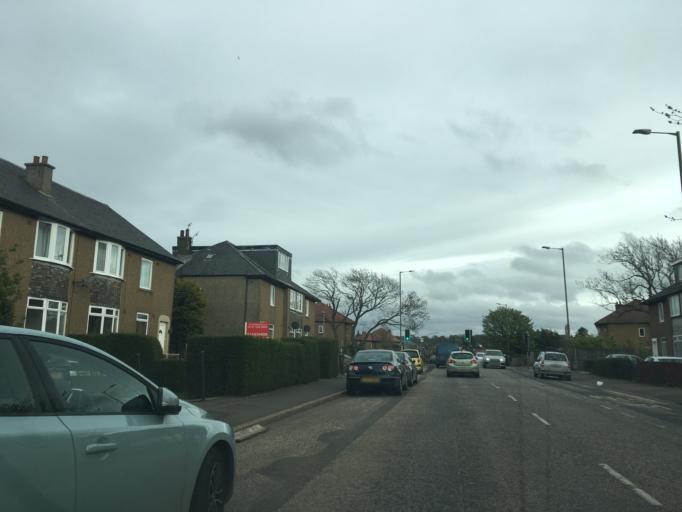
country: GB
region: Scotland
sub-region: Edinburgh
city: Colinton
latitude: 55.9104
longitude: -3.2358
